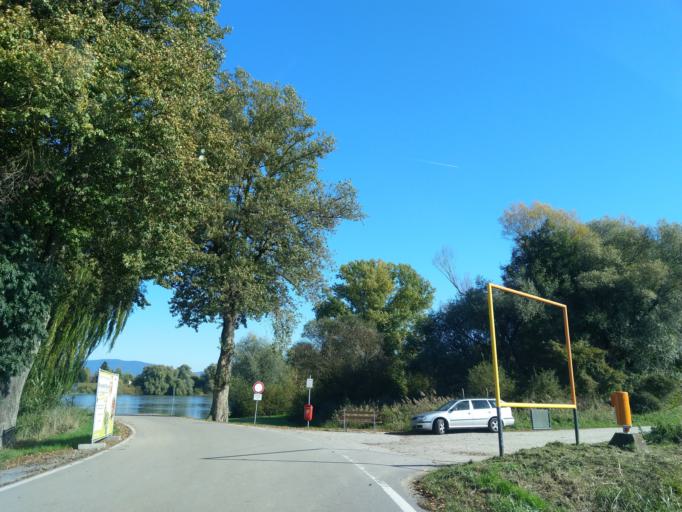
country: DE
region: Bavaria
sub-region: Lower Bavaria
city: Stephansposching
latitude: 48.8227
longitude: 12.8066
